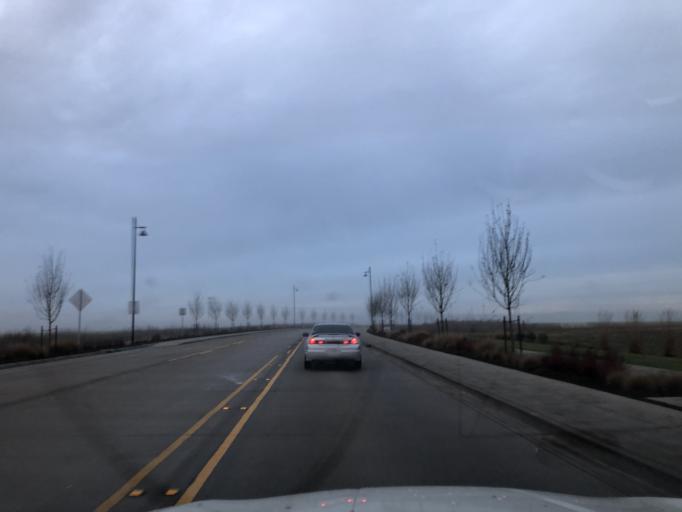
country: US
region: Oregon
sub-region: Washington County
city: Aloha
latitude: 45.4922
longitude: -122.8927
